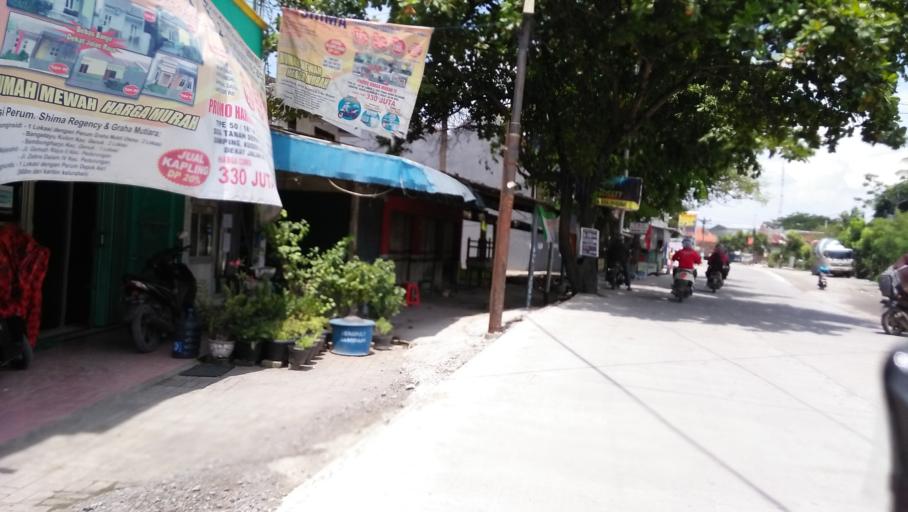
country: ID
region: Central Java
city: Mranggen
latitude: -6.9785
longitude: 110.4803
